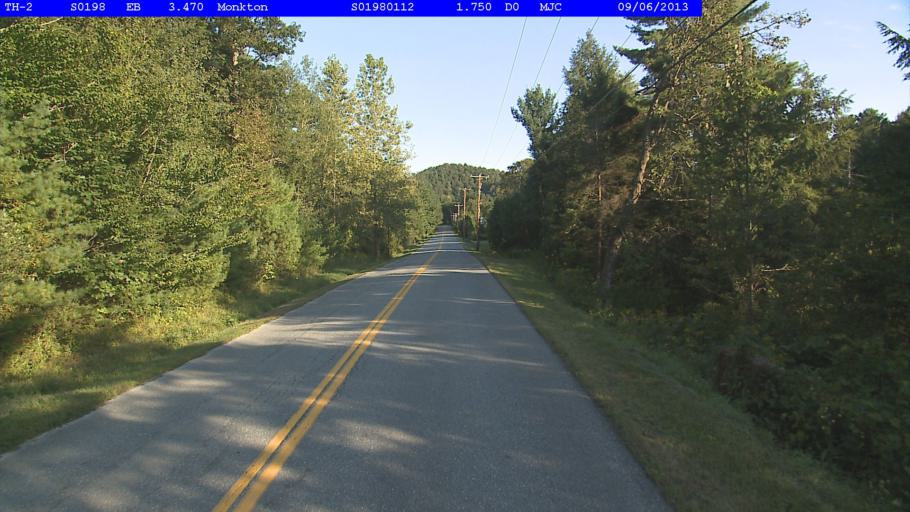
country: US
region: Vermont
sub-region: Chittenden County
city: Hinesburg
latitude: 44.2452
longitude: -73.1658
